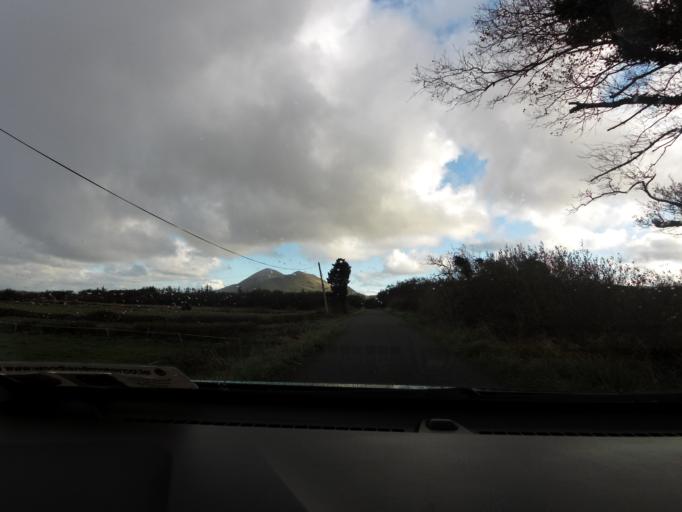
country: IE
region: Connaught
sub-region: Maigh Eo
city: Westport
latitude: 53.7733
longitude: -9.7697
